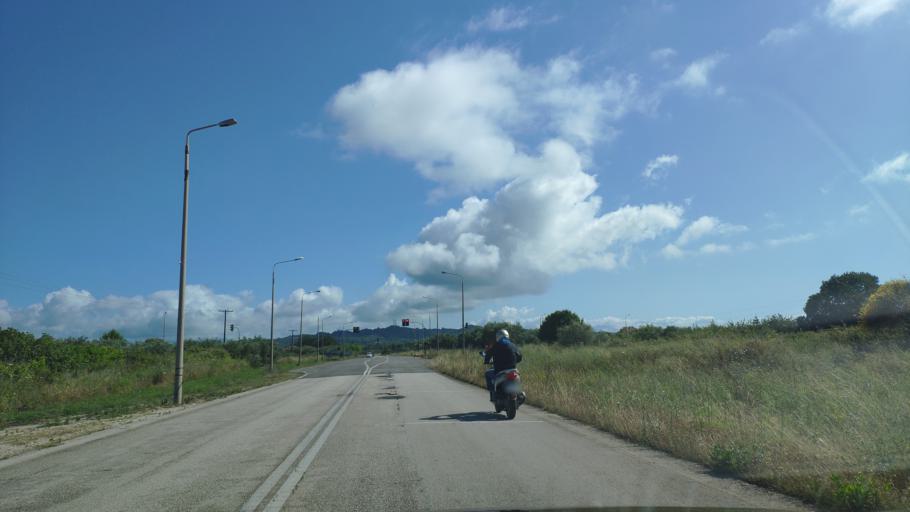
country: GR
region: Epirus
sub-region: Nomos Prevezis
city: Preveza
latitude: 39.0012
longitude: 20.7167
